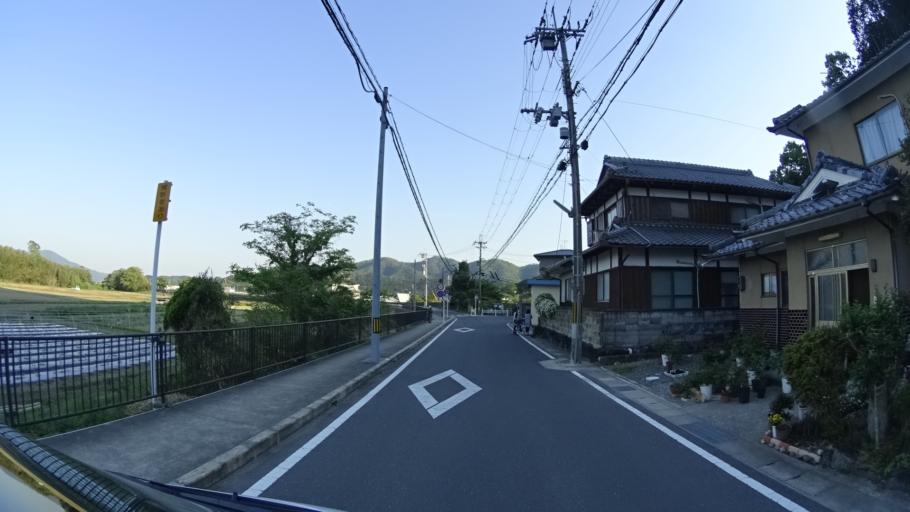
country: JP
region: Kyoto
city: Kameoka
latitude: 35.0822
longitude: 135.5167
